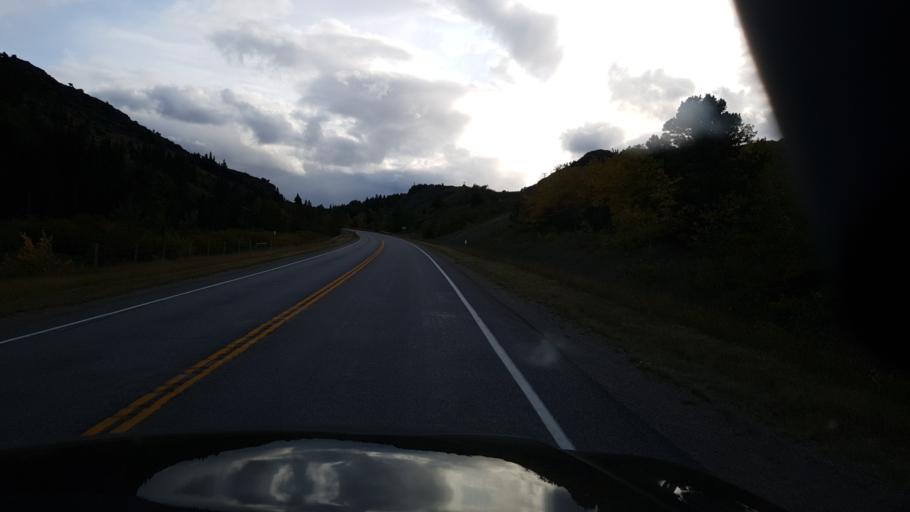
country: US
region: Montana
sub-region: Glacier County
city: South Browning
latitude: 48.4017
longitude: -113.2501
